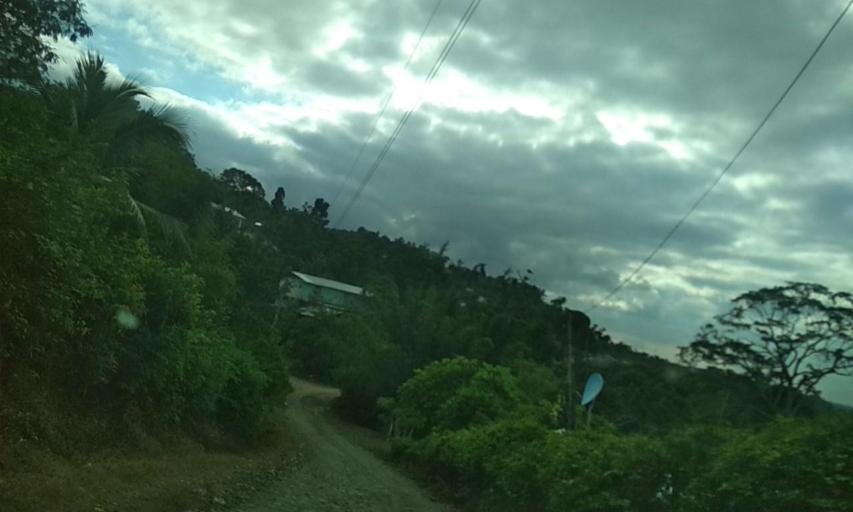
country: MX
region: Veracruz
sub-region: Papantla
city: Polutla
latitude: 20.5756
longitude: -97.2509
